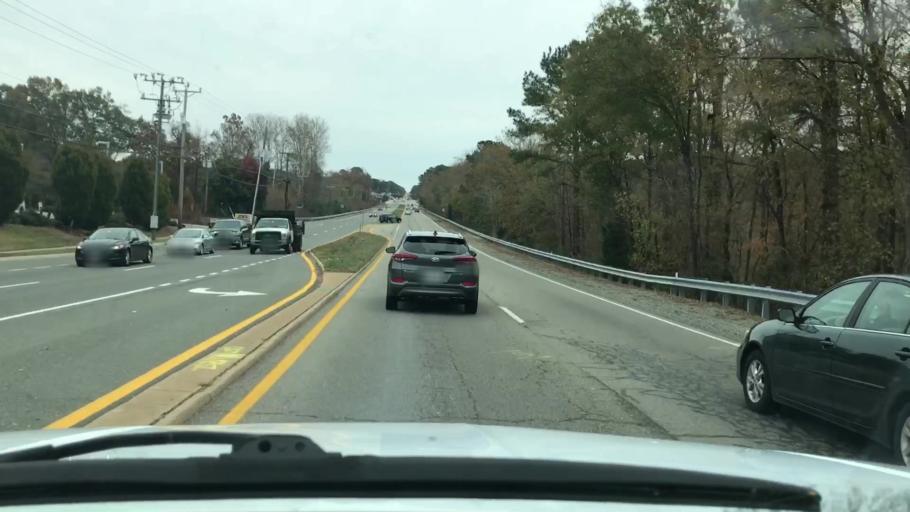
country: US
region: Virginia
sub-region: Henrico County
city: Short Pump
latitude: 37.5974
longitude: -77.6172
